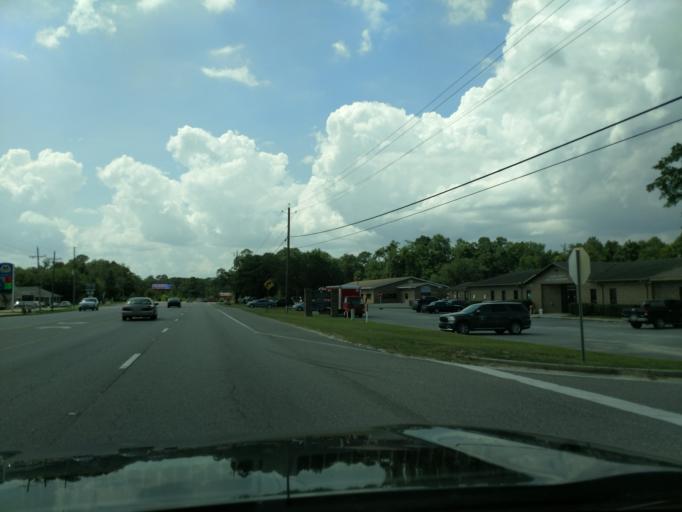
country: US
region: Mississippi
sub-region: Jackson County
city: Gulf Hills
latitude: 30.4415
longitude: -88.8368
